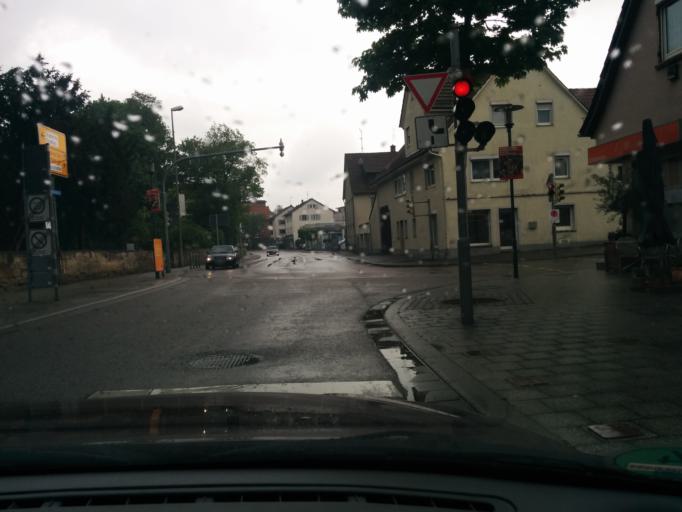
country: DE
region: Baden-Wuerttemberg
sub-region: Regierungsbezirk Stuttgart
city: Ditzingen
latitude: 48.8275
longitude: 9.0685
